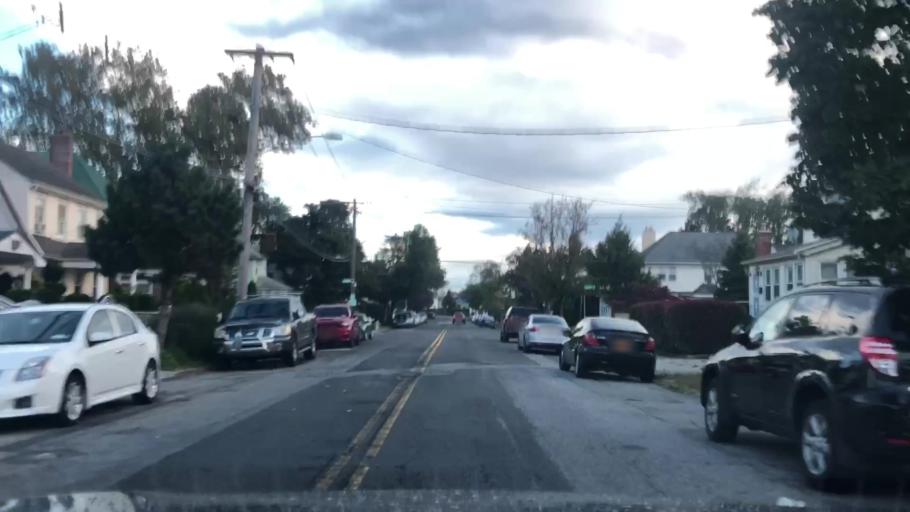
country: US
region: New York
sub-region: Nassau County
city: Bellerose Terrace
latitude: 40.7132
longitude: -73.7316
